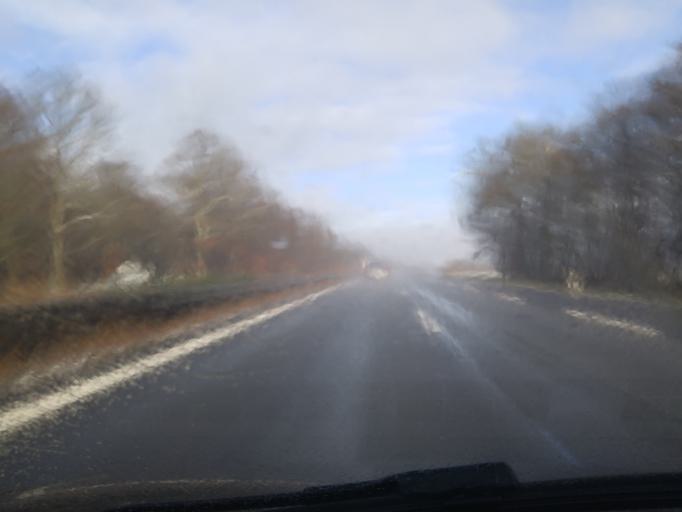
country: DE
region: Bavaria
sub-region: Regierungsbezirk Unterfranken
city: Arnstein
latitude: 49.9281
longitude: 9.9986
